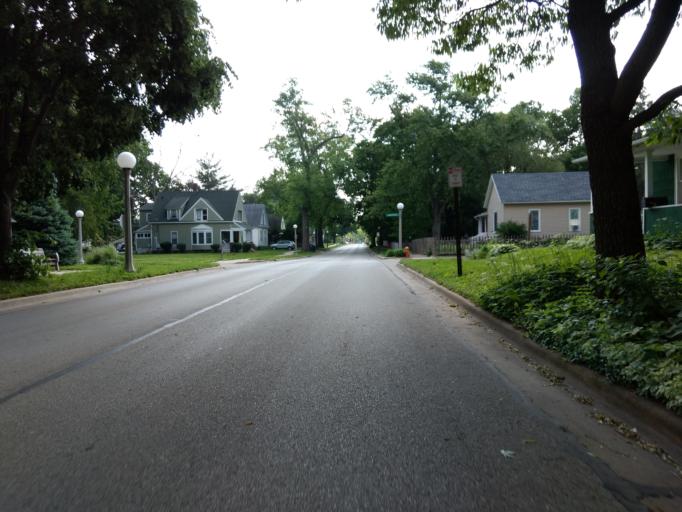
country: US
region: Illinois
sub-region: Champaign County
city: Urbana
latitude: 40.1108
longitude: -88.2007
